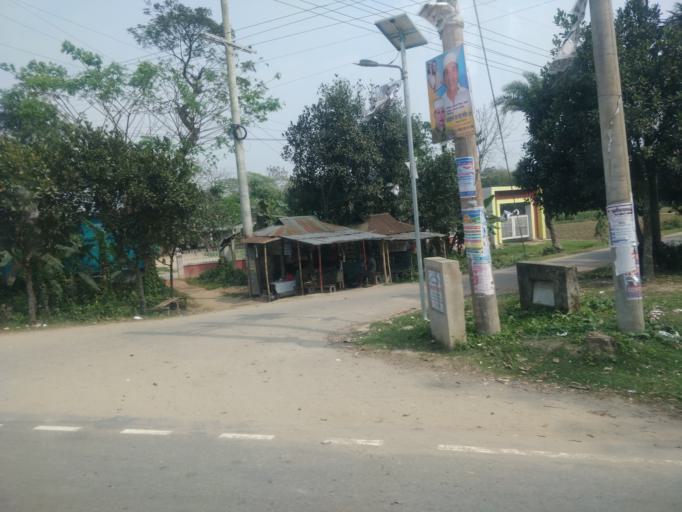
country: BD
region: Sylhet
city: Habiganj
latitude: 24.3144
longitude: 91.4368
